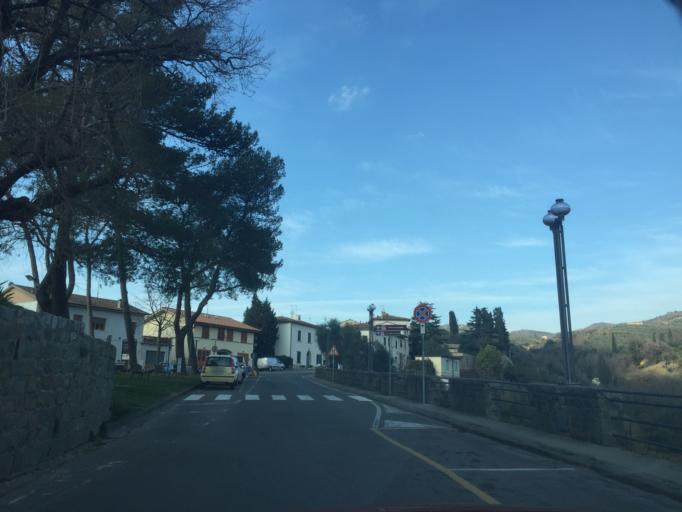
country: IT
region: Tuscany
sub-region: Province of Florence
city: Vinci
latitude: 43.7882
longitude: 10.9282
